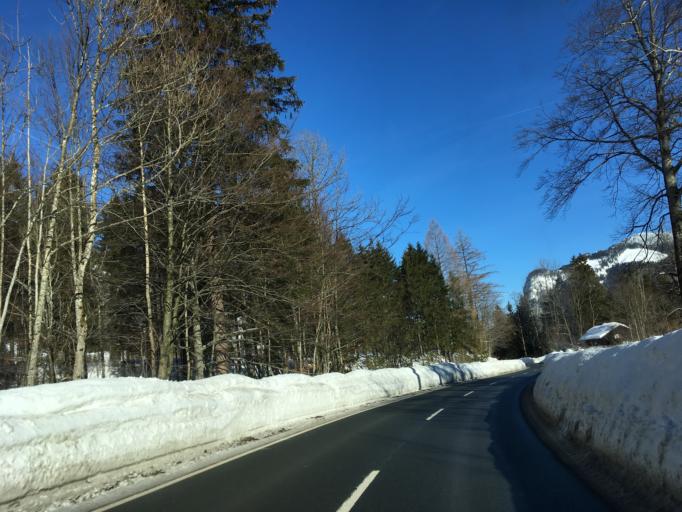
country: AT
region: Tyrol
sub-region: Politischer Bezirk Kufstein
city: Rettenschoss
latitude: 47.7140
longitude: 12.2852
